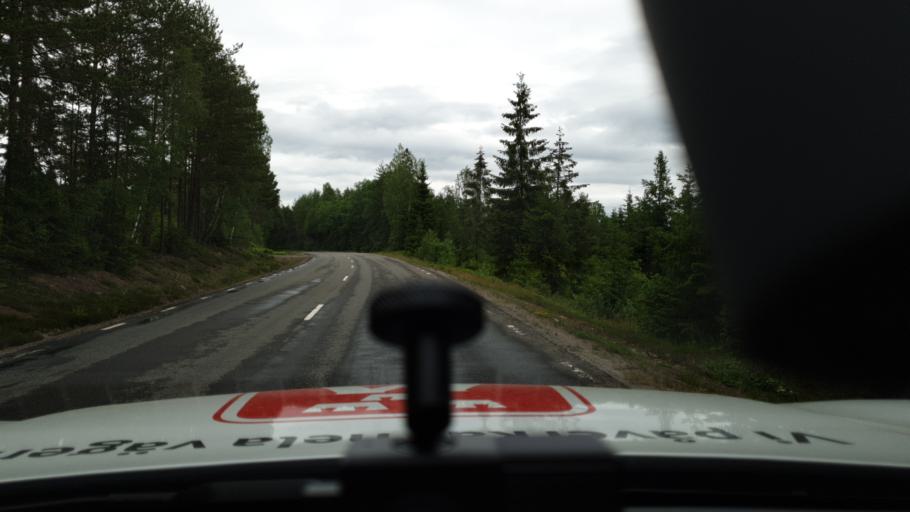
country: SE
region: Joenkoeping
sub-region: Mullsjo Kommun
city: Mullsjoe
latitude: 57.9819
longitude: 13.8096
